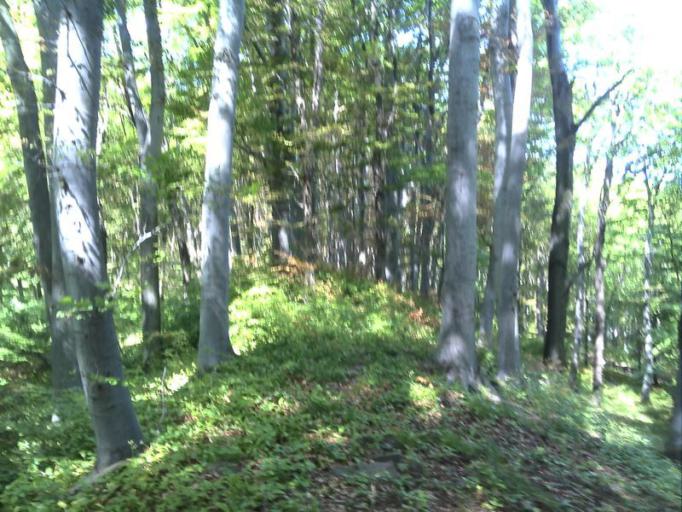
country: HU
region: Baranya
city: Pellerd
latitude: 46.0975
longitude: 18.1410
